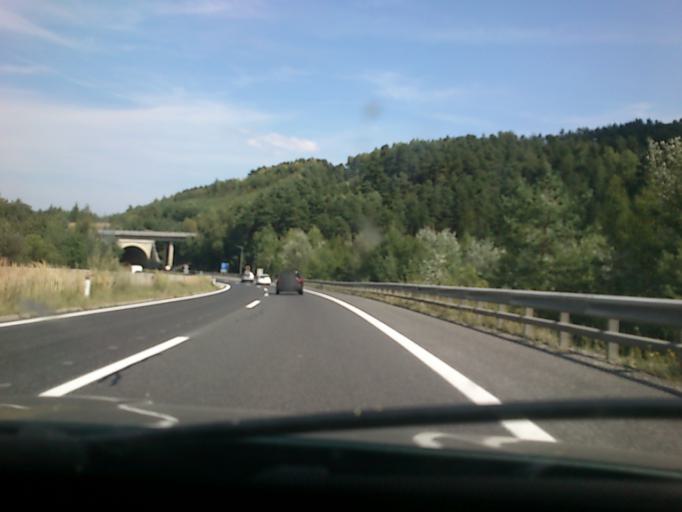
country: AT
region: Lower Austria
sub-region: Politischer Bezirk Neunkirchen
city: Thomasberg
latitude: 47.5681
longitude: 16.1152
